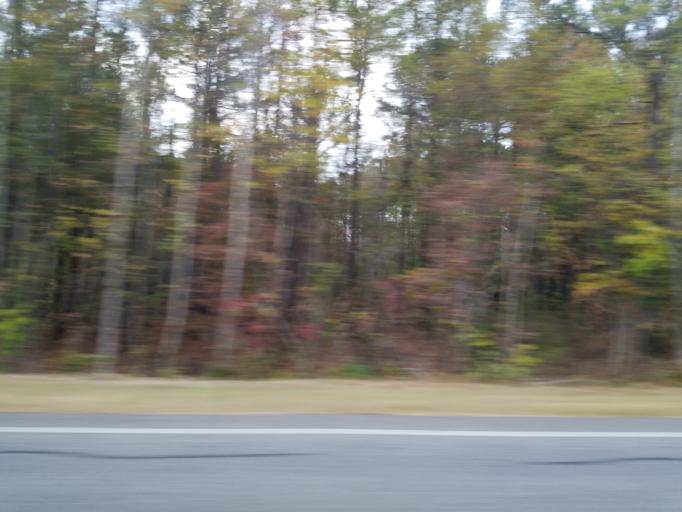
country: US
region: Georgia
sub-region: Murray County
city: Chatsworth
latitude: 34.5908
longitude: -84.6994
